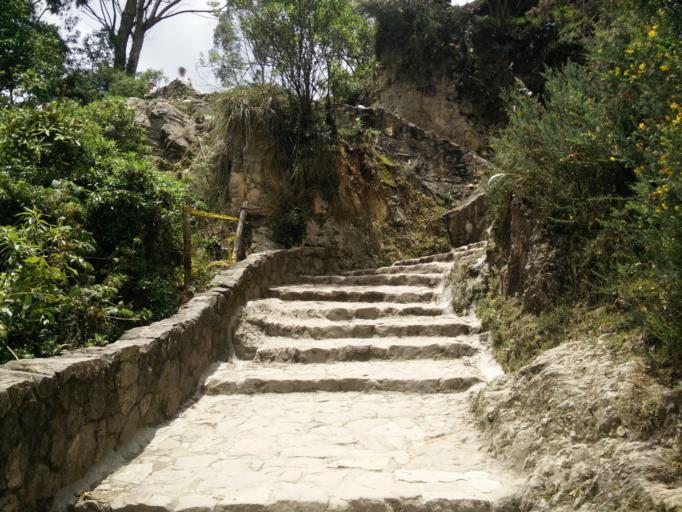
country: CO
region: Bogota D.C.
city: Bogota
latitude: 4.6103
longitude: -74.0552
